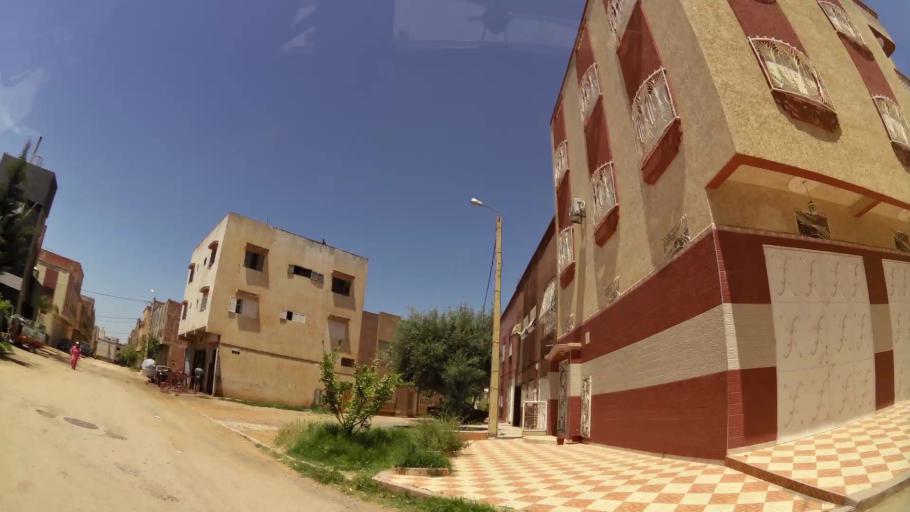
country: MA
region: Rabat-Sale-Zemmour-Zaer
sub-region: Khemisset
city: Khemisset
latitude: 33.8309
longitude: -6.0801
